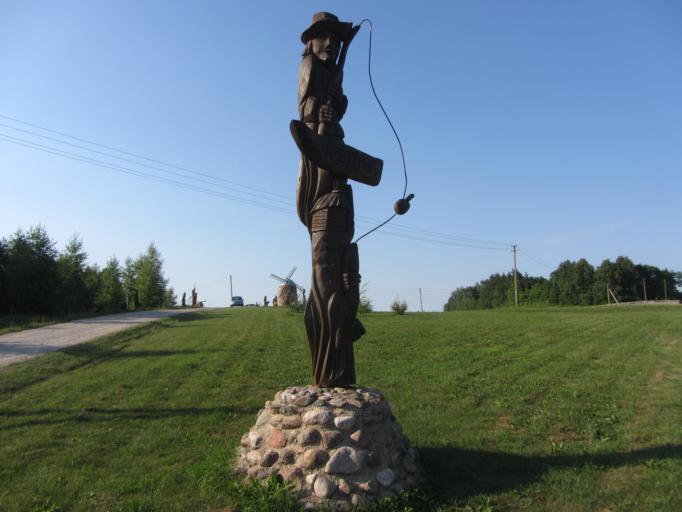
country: LT
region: Utenos apskritis
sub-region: Anyksciai
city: Anyksciai
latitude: 55.4854
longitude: 25.3087
